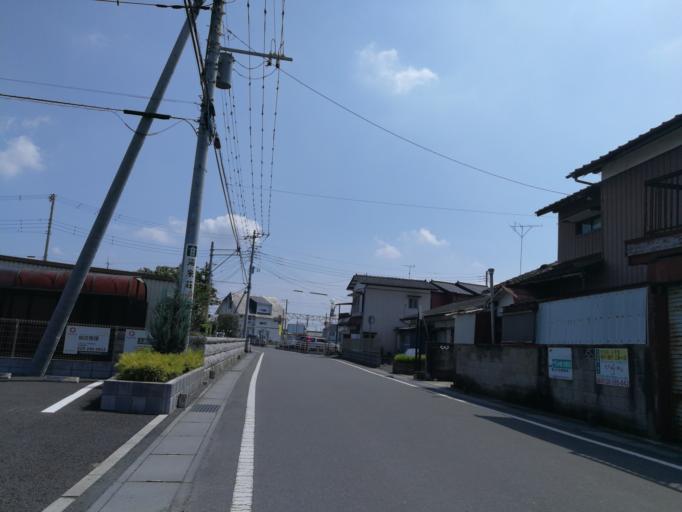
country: JP
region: Ibaraki
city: Tomobe
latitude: 36.3703
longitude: 140.3509
